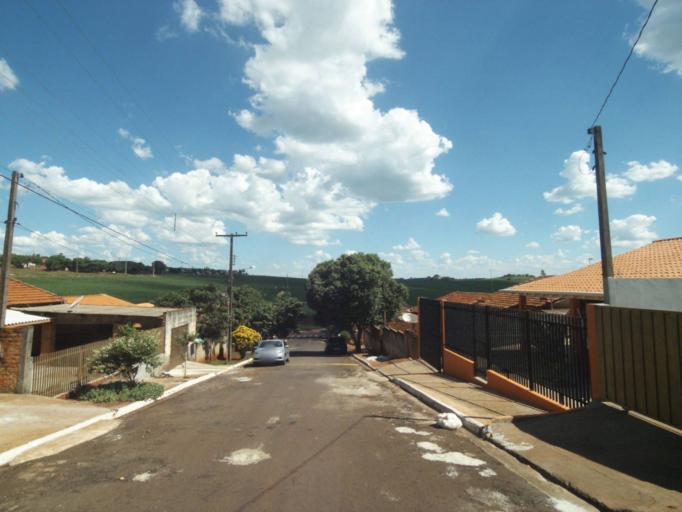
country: BR
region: Parana
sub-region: Sertanopolis
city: Sertanopolis
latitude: -23.0455
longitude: -50.8214
